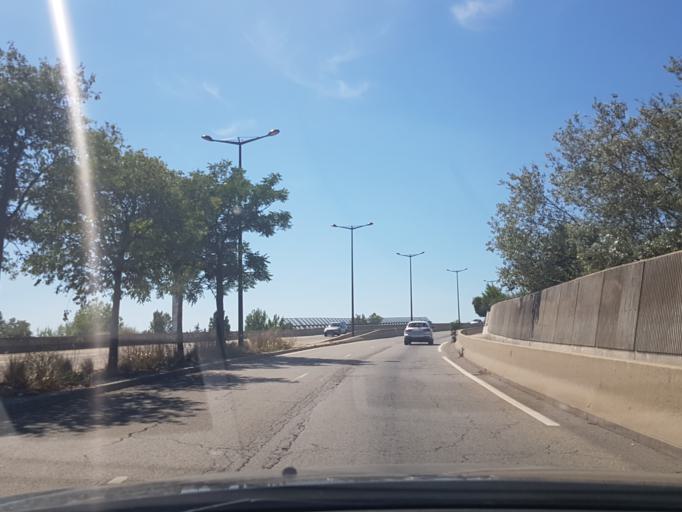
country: FR
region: Provence-Alpes-Cote d'Azur
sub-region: Departement du Vaucluse
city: Avignon
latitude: 43.9270
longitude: 4.8000
